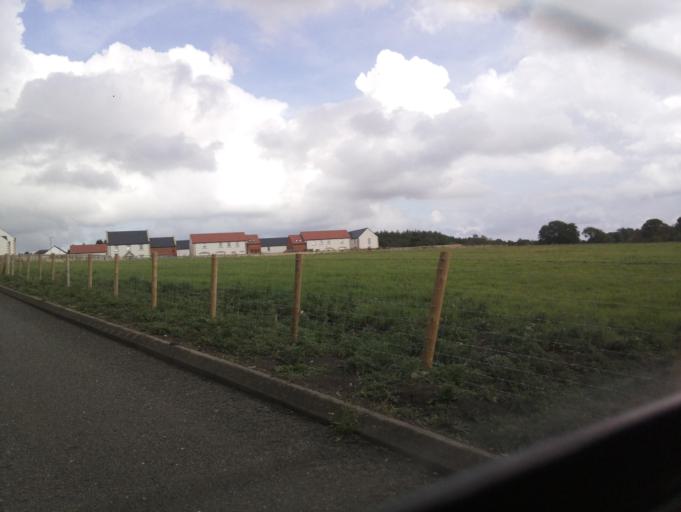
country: GB
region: England
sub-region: County Durham
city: Hamsterley
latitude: 54.7001
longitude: -1.7838
